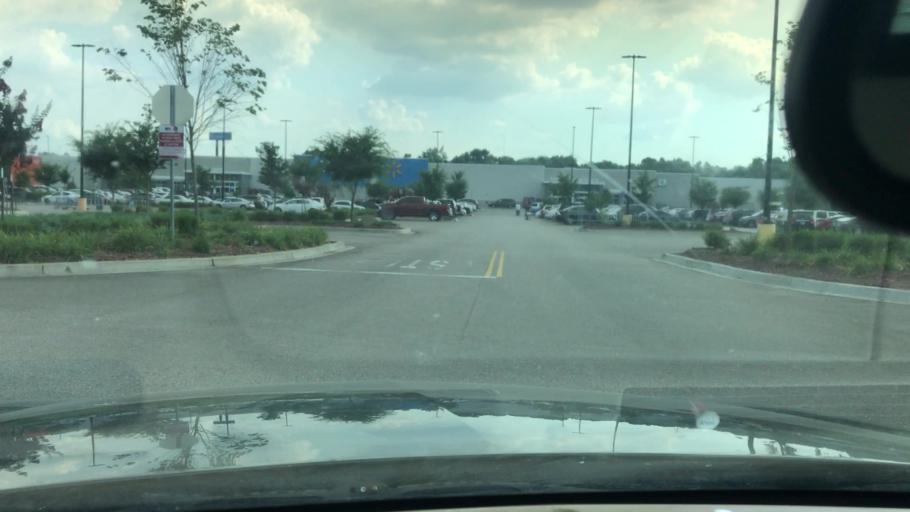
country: US
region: Tennessee
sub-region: Shelby County
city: Bartlett
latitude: 35.1778
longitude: -89.8379
